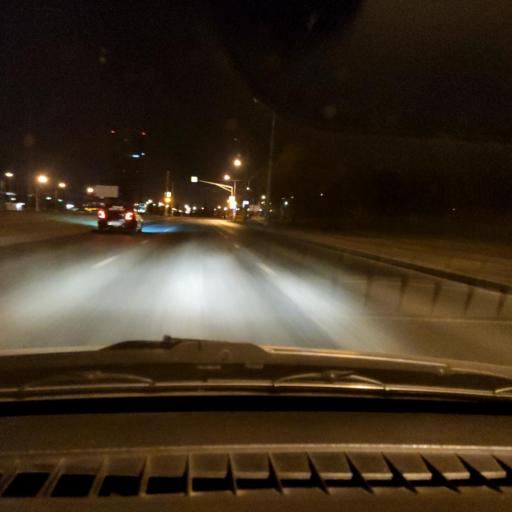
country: RU
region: Samara
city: Tol'yatti
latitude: 53.5559
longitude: 49.2548
